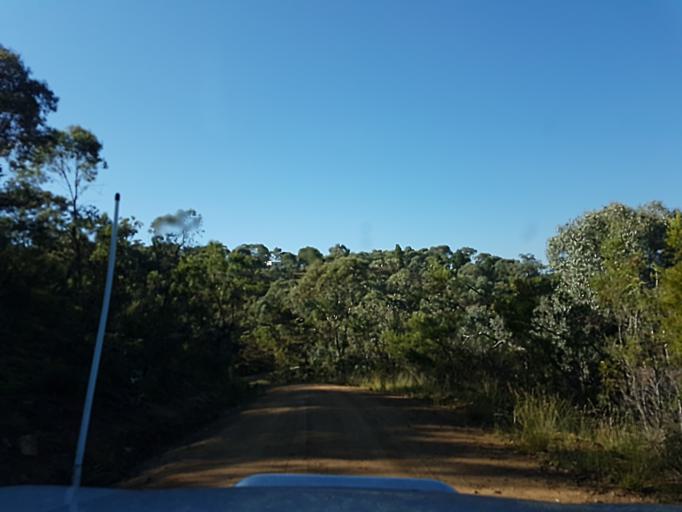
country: AU
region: New South Wales
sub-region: Snowy River
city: Jindabyne
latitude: -36.9349
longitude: 148.3397
